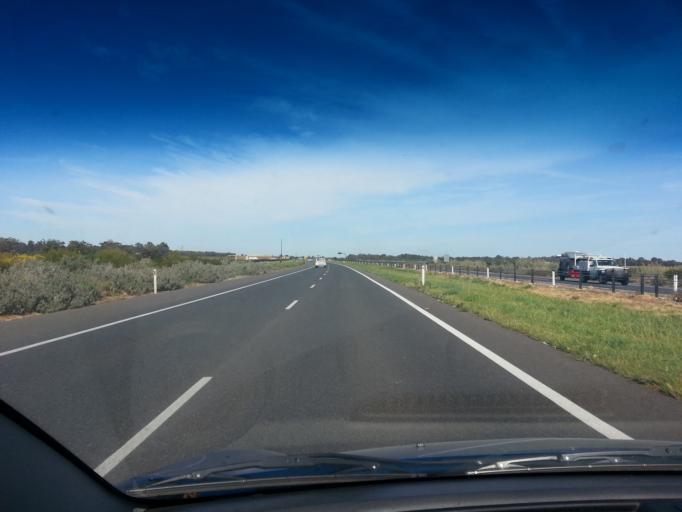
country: AU
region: South Australia
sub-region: Playford
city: Angle Vale
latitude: -34.6636
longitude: 138.6545
